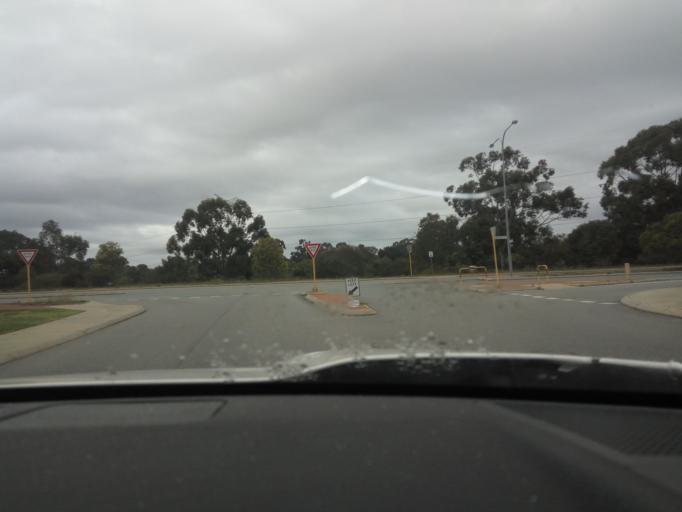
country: AU
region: Western Australia
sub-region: City of Cockburn
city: City of Cockburn
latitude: -32.1102
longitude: 115.8487
